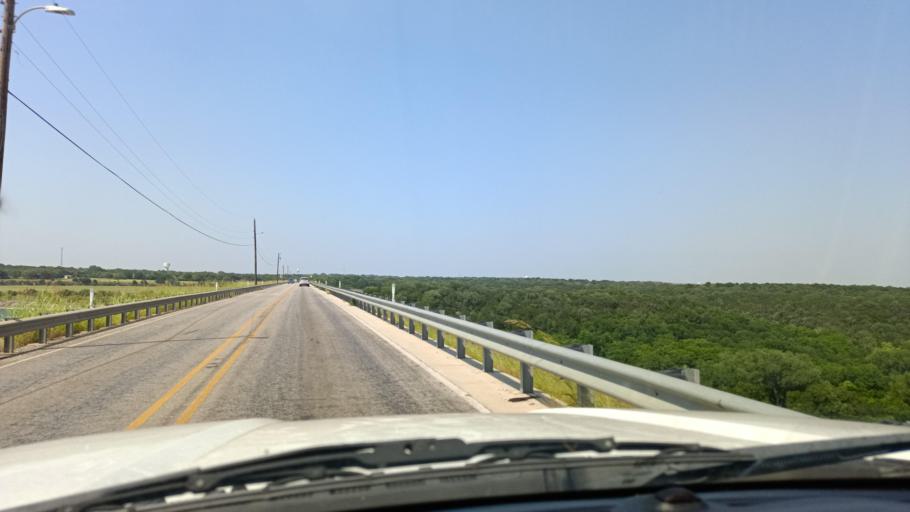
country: US
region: Texas
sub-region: Bell County
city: Morgans Point Resort
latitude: 31.1071
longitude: -97.4732
